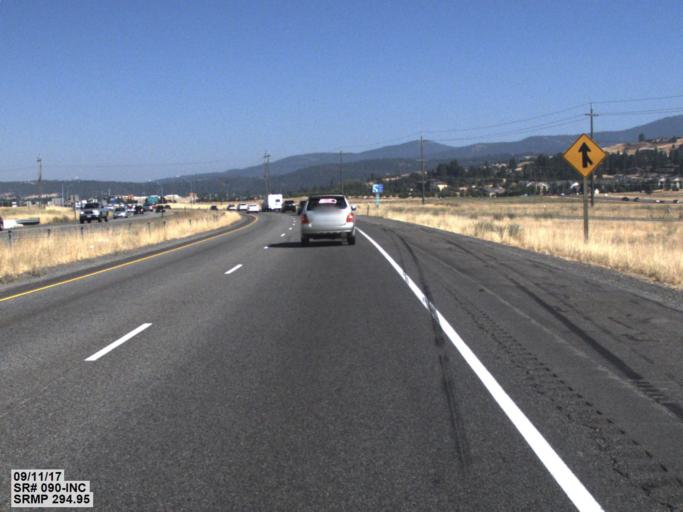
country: US
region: Washington
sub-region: Spokane County
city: Liberty Lake
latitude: 47.6655
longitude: -117.1325
